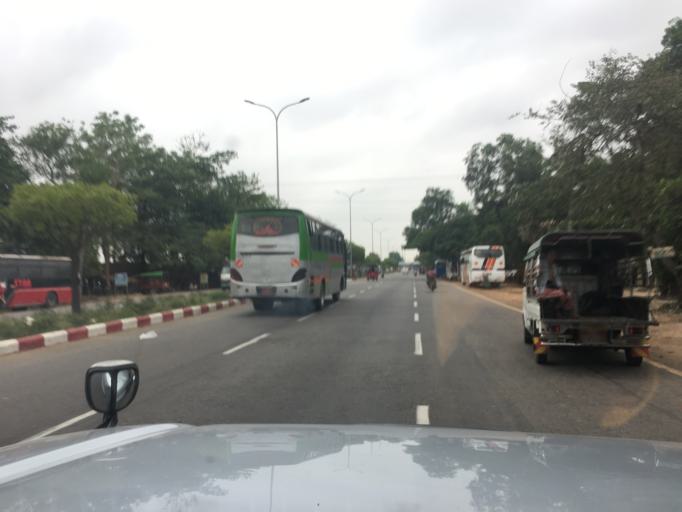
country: MM
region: Bago
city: Bago
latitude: 17.2502
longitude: 96.4673
